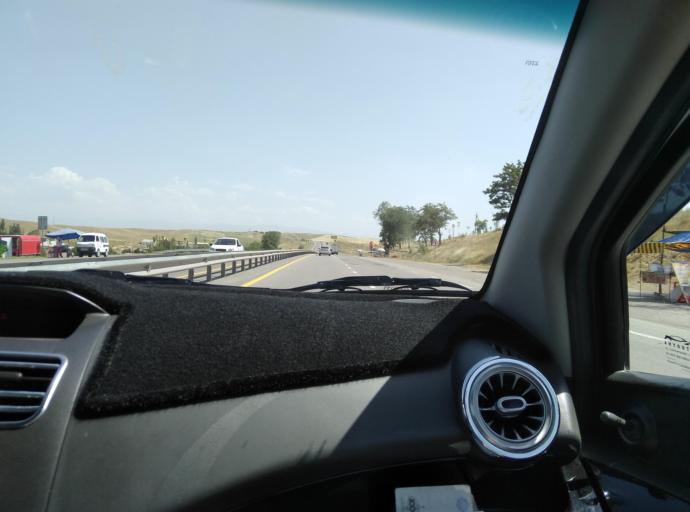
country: UZ
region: Toshkent
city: Ohangaron
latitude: 40.9761
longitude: 69.5436
